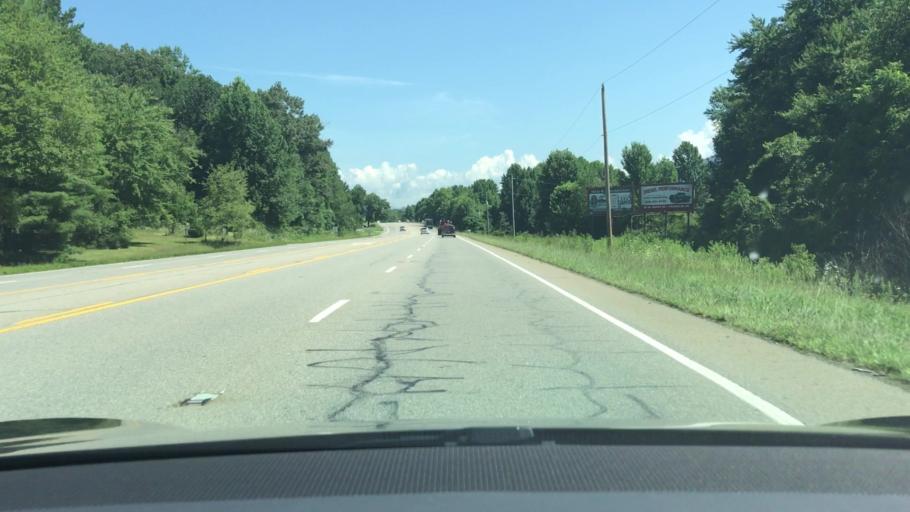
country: US
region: North Carolina
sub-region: Macon County
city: Franklin
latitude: 35.0734
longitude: -83.3861
